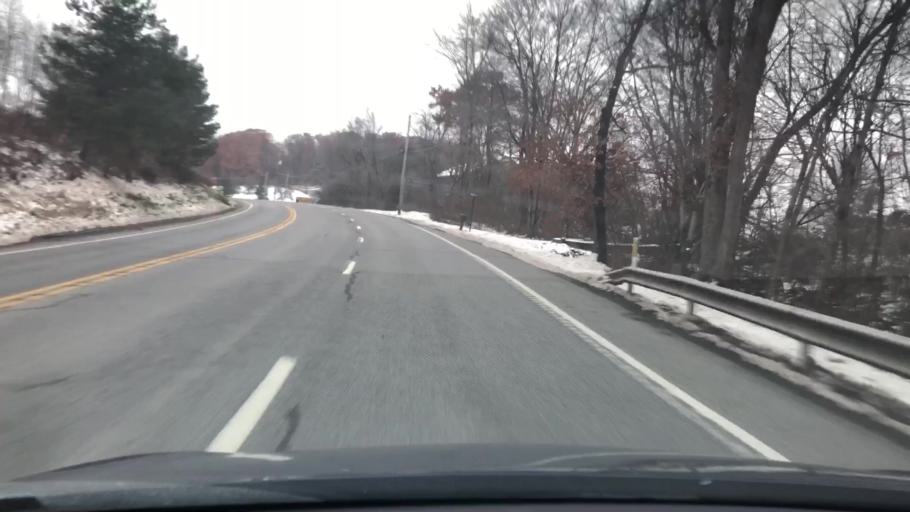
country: US
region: Pennsylvania
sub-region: Jefferson County
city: Brookville
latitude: 41.1492
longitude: -79.1232
